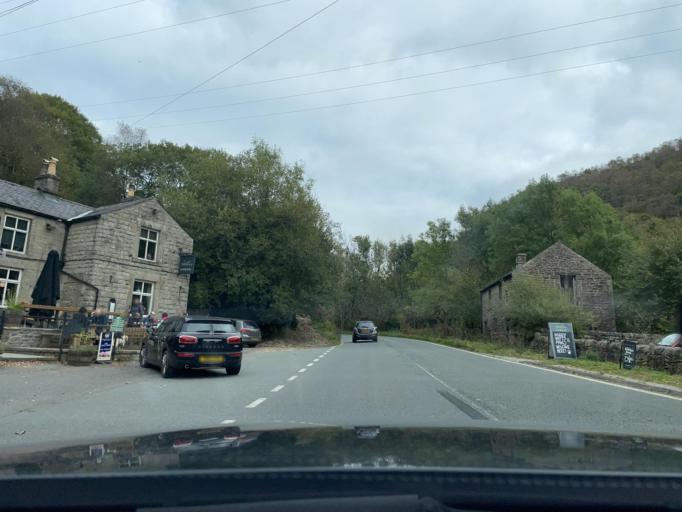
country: GB
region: England
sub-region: Derbyshire
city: Hope Valley
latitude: 53.3750
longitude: -1.6941
